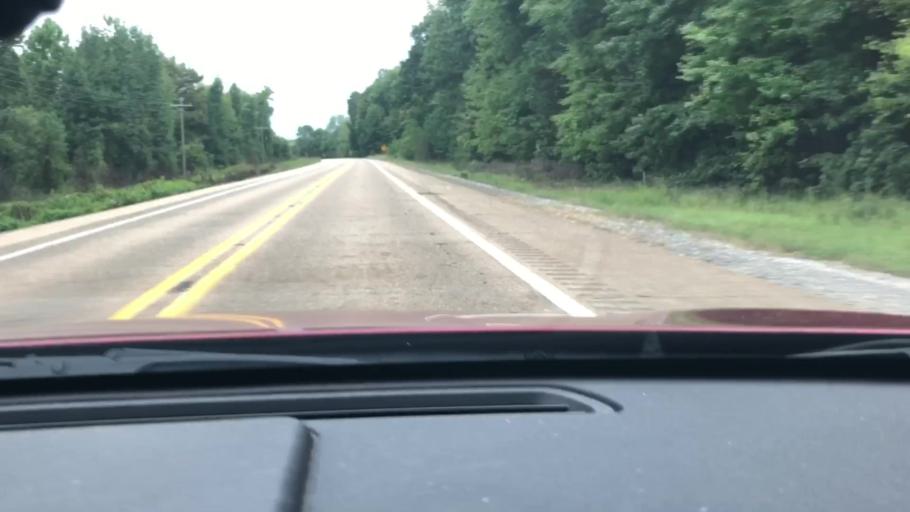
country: US
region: Arkansas
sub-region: Miller County
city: Texarkana
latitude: 33.4165
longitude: -93.8123
